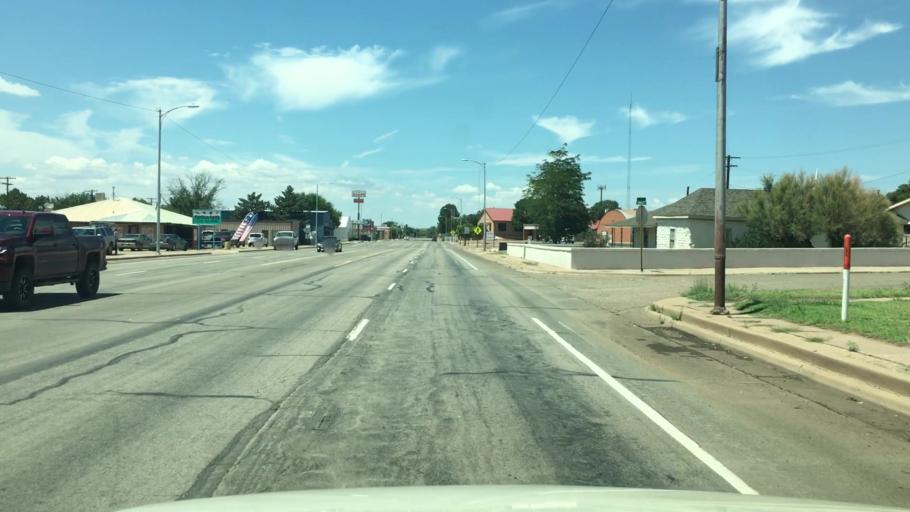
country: US
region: New Mexico
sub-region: De Baca County
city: Fort Sumner
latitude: 34.4701
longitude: -104.2402
